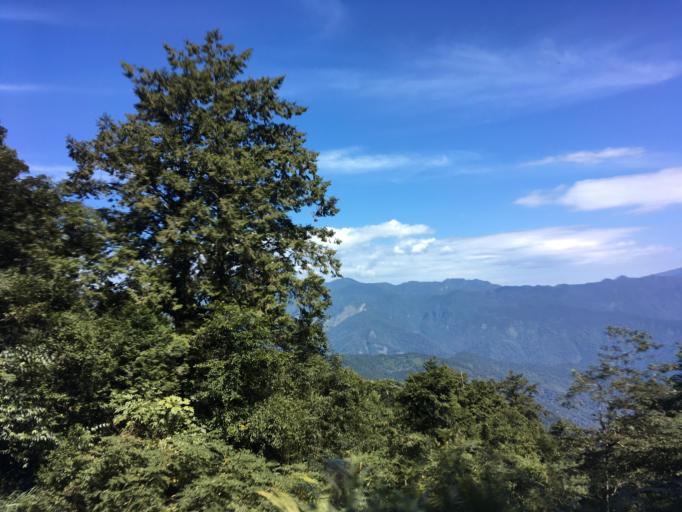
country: TW
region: Taiwan
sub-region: Yilan
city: Yilan
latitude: 24.5253
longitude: 121.5168
